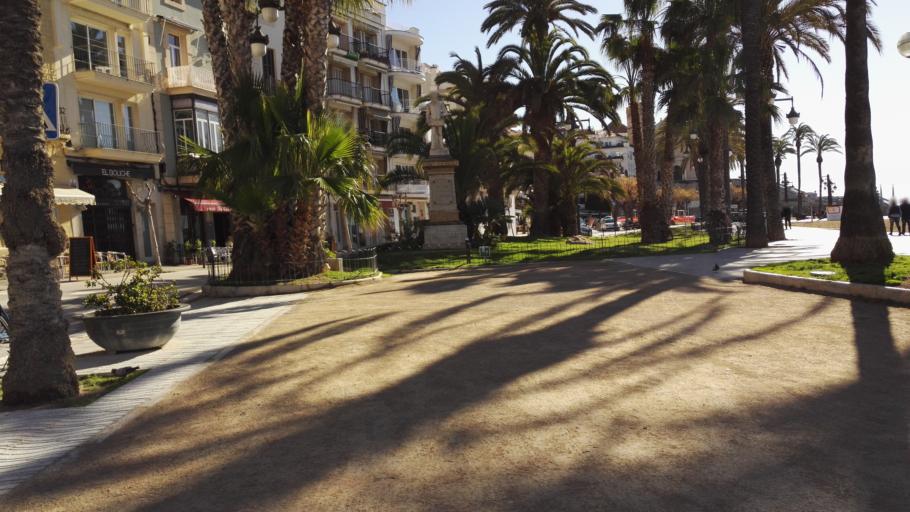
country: ES
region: Catalonia
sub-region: Provincia de Barcelona
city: Sitges
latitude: 41.2350
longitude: 1.8089
